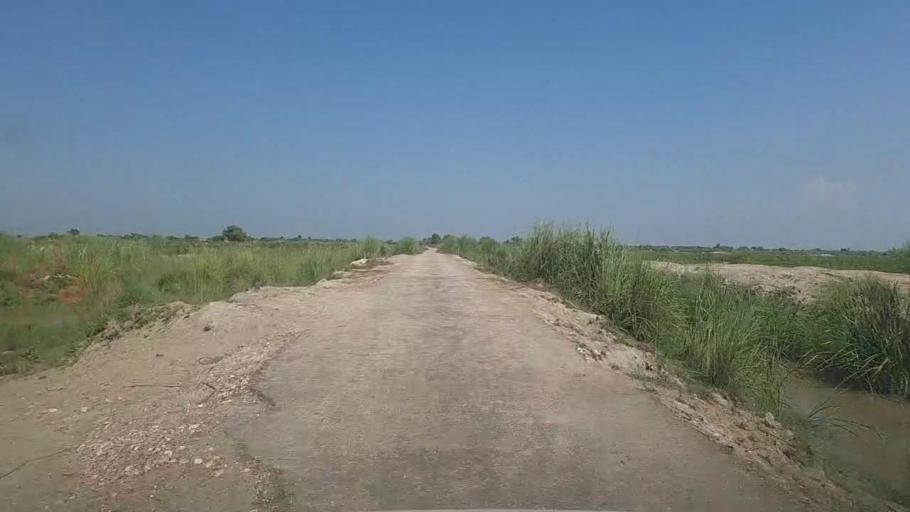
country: PK
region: Sindh
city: Kandhkot
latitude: 28.2979
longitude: 69.2093
